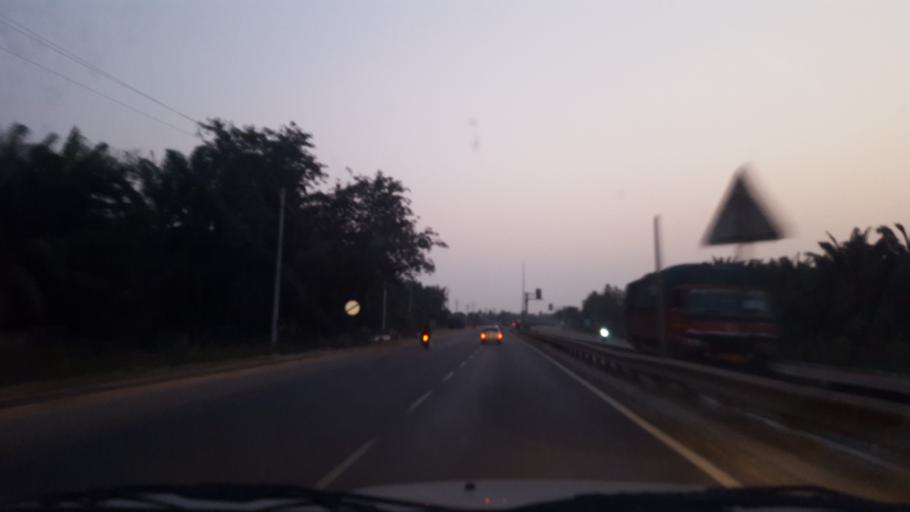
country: IN
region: Andhra Pradesh
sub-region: East Godavari
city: Peddapuram
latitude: 17.1547
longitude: 81.9889
